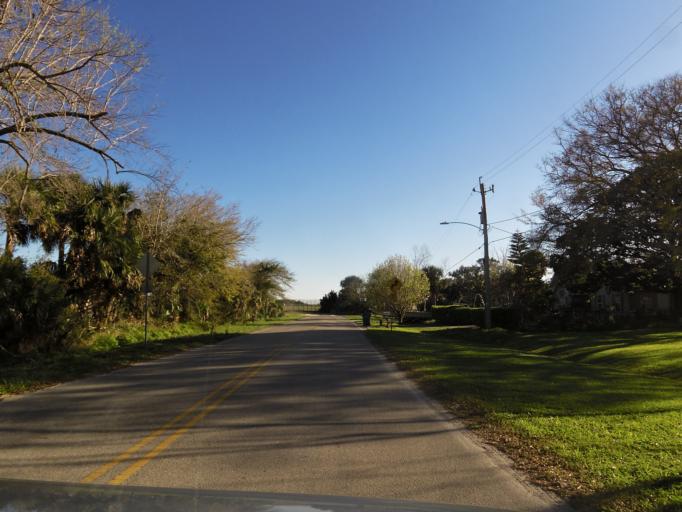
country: US
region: Florida
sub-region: Duval County
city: Atlantic Beach
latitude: 30.3932
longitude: -81.4267
